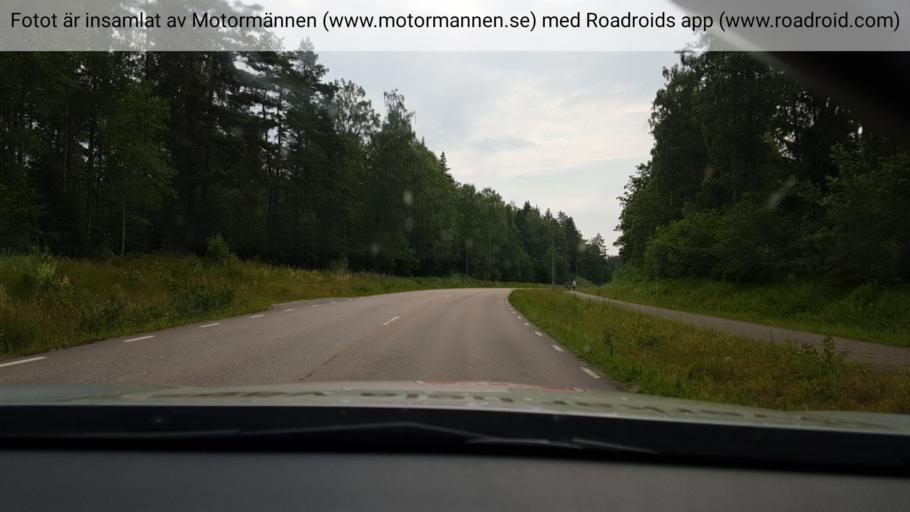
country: SE
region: Vaestra Goetaland
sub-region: Skovde Kommun
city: Skultorp
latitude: 58.3417
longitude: 13.8538
